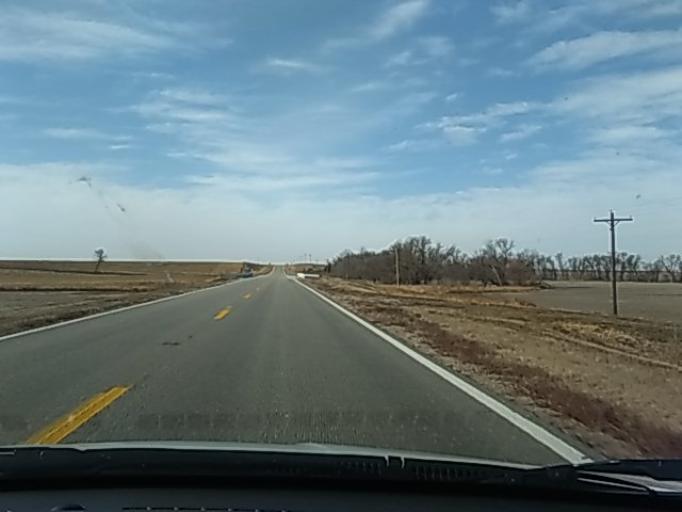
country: US
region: Nebraska
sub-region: Clay County
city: Clay Center
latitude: 40.4233
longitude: -98.0244
